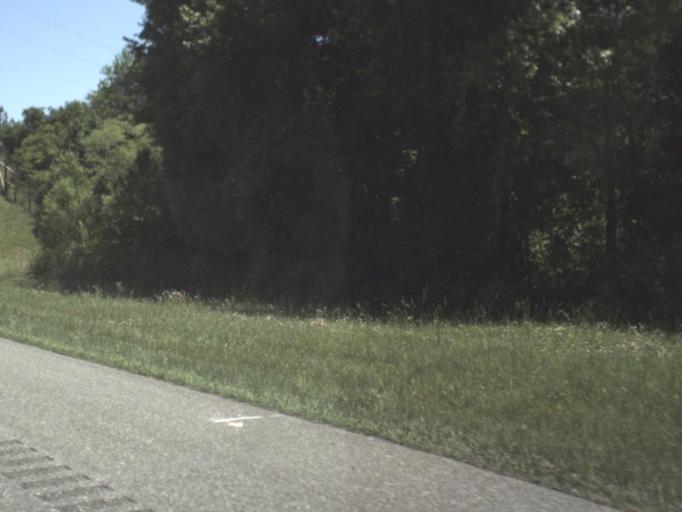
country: US
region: Florida
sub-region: Jefferson County
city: Monticello
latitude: 30.4724
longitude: -83.8242
